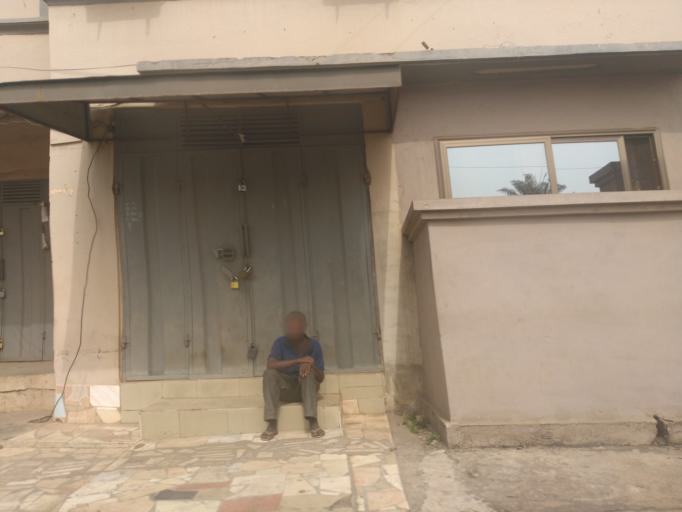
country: GH
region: Ashanti
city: Kumasi
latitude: 6.7060
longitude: -1.6183
